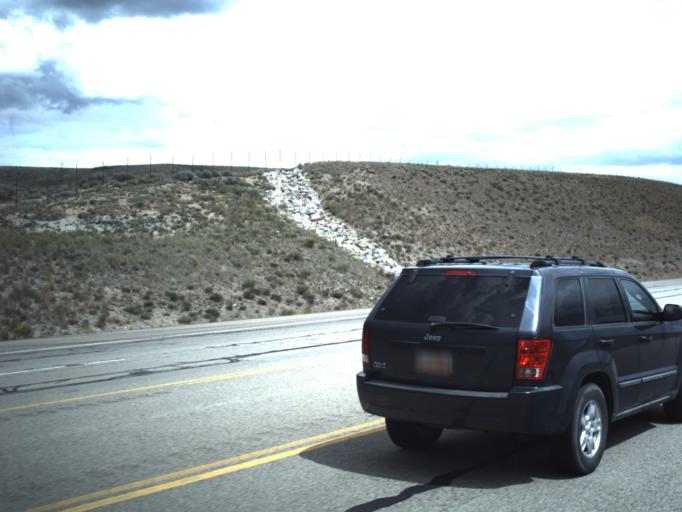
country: US
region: Utah
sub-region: Carbon County
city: Helper
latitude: 39.8526
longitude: -111.0134
